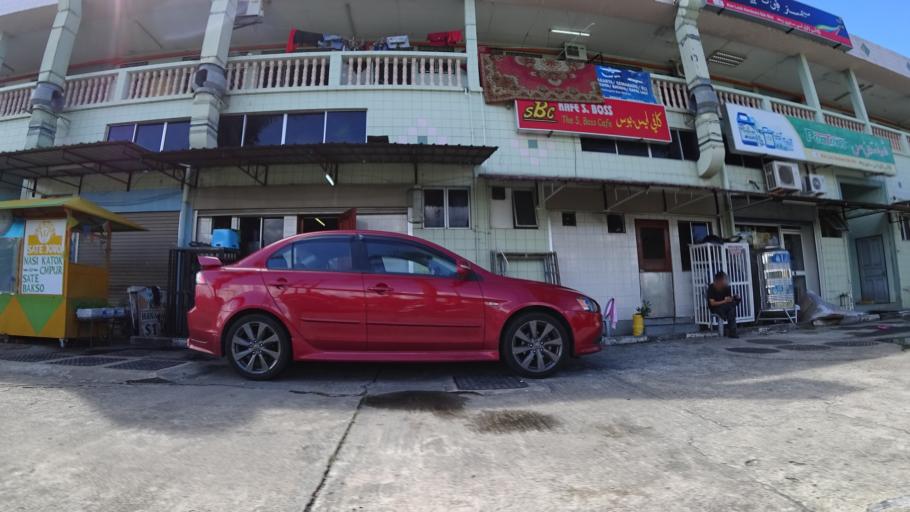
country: BN
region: Brunei and Muara
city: Bandar Seri Begawan
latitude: 4.8419
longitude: 114.8729
